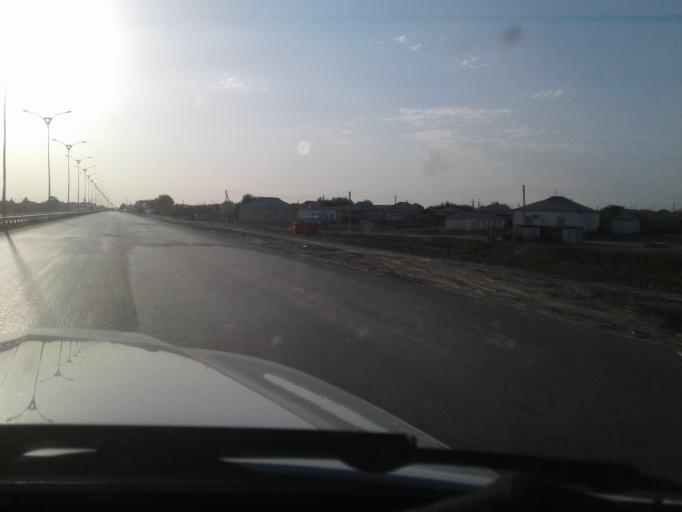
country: TM
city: Murgab
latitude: 37.4888
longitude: 61.9872
